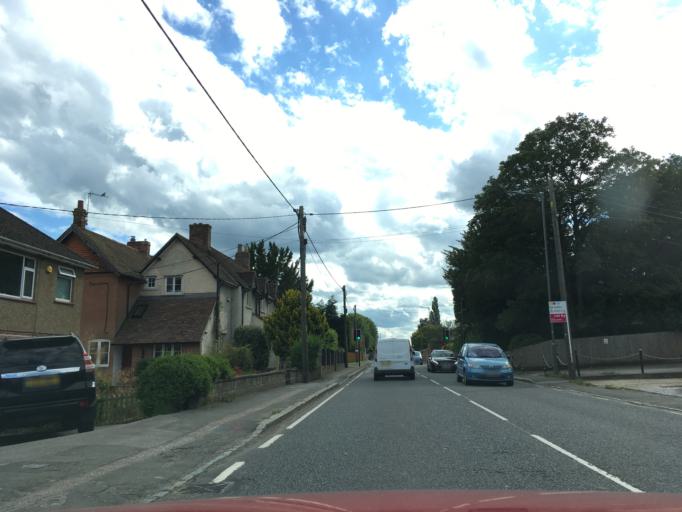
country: GB
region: England
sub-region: Buckinghamshire
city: Aylesbury
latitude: 51.8312
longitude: -0.7865
